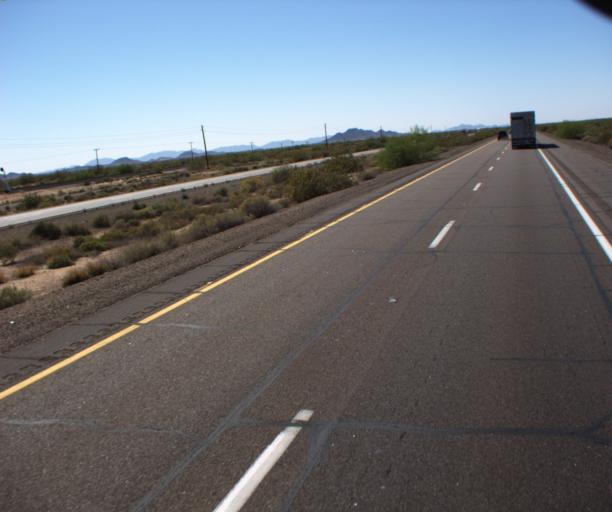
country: US
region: Arizona
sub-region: Maricopa County
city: Gila Bend
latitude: 32.8322
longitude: -113.3849
